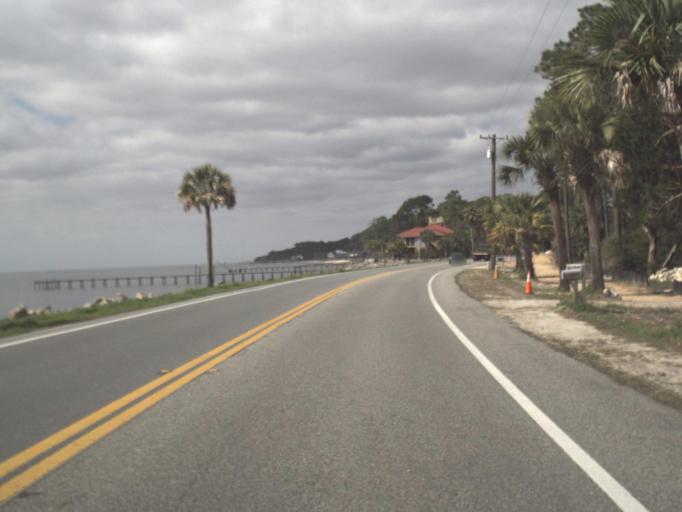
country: US
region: Florida
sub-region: Franklin County
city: Carrabelle
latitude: 29.8268
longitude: -84.6975
